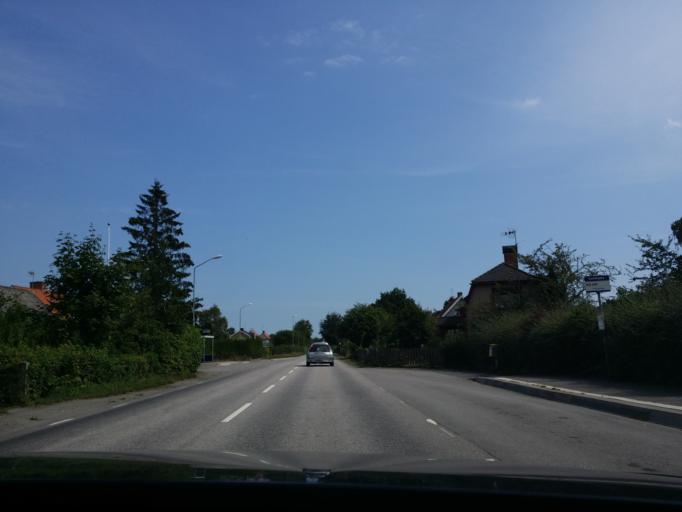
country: SE
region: Blekinge
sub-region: Solvesborgs Kommun
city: Soelvesborg
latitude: 56.0455
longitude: 14.6775
